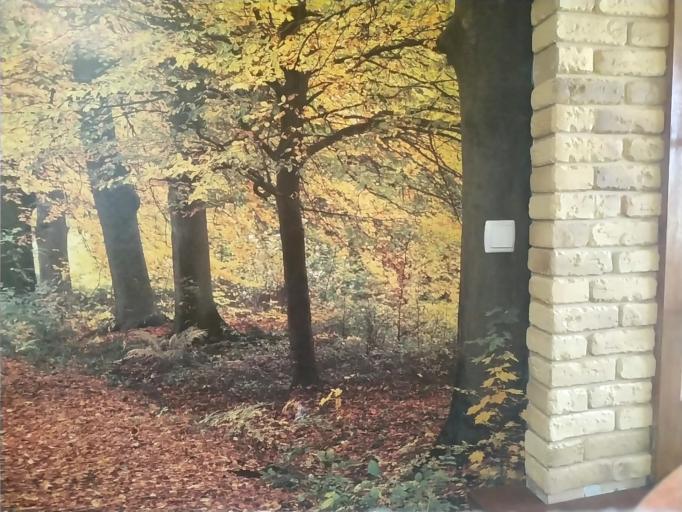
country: RU
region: Tverskaya
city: Krasnomayskiy
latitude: 57.7138
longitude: 34.4803
